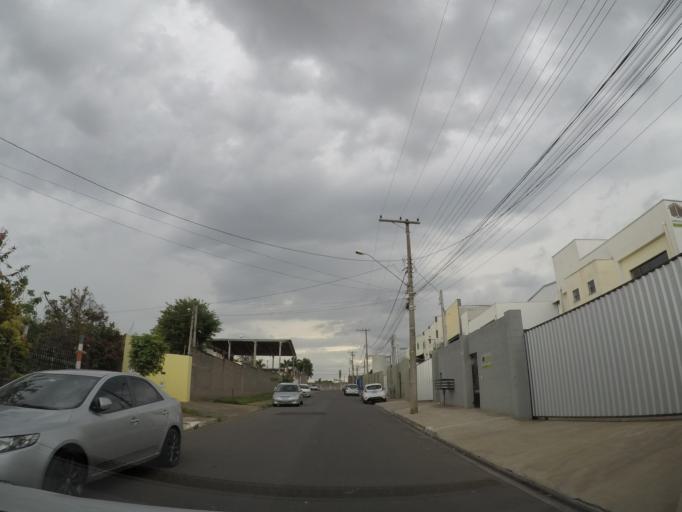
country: BR
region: Sao Paulo
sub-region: Sumare
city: Sumare
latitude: -22.8129
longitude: -47.2454
